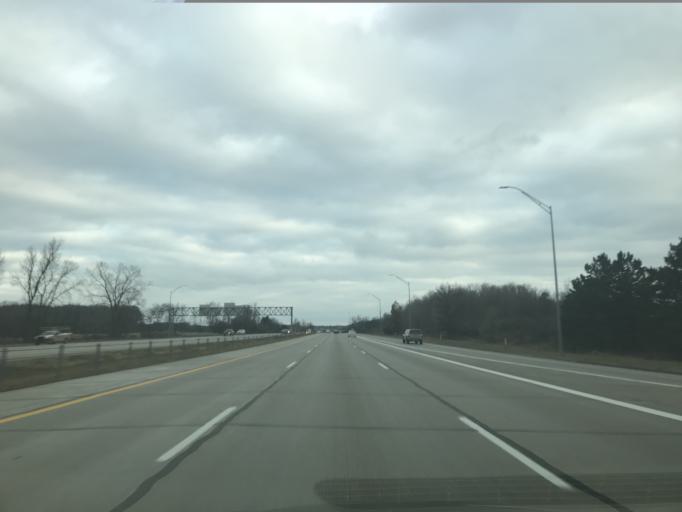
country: US
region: Michigan
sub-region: Eaton County
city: Waverly
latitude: 42.7445
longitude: -84.6679
